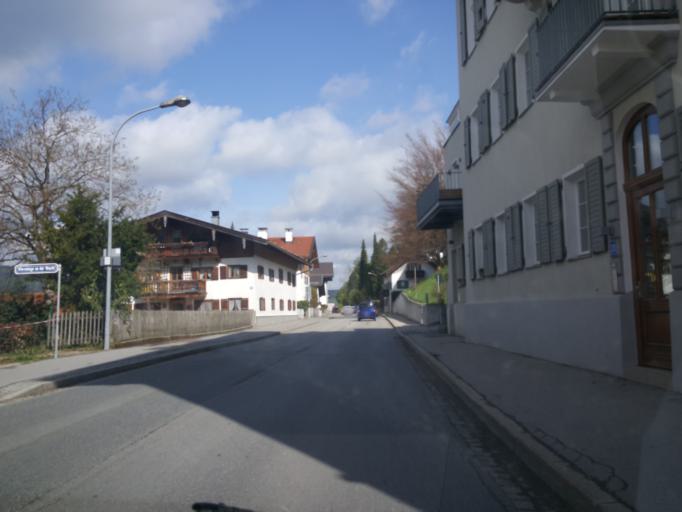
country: DE
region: Bavaria
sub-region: Upper Bavaria
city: Tegernsee
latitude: 47.7180
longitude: 11.7520
